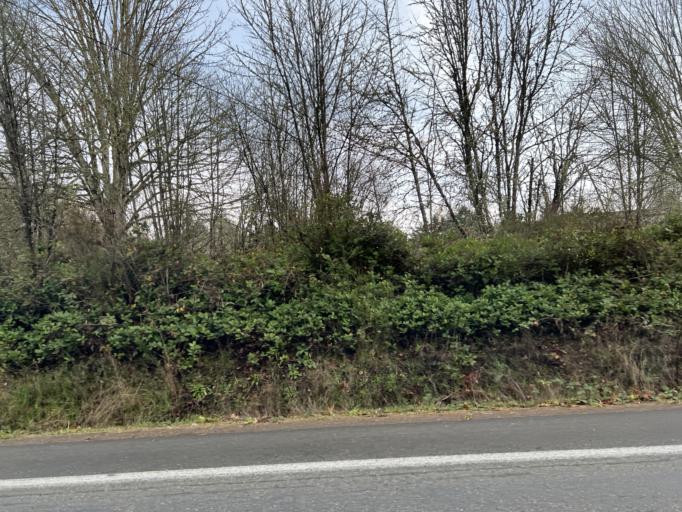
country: US
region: Washington
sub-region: Kitsap County
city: Bainbridge Island
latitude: 47.6554
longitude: -122.5188
